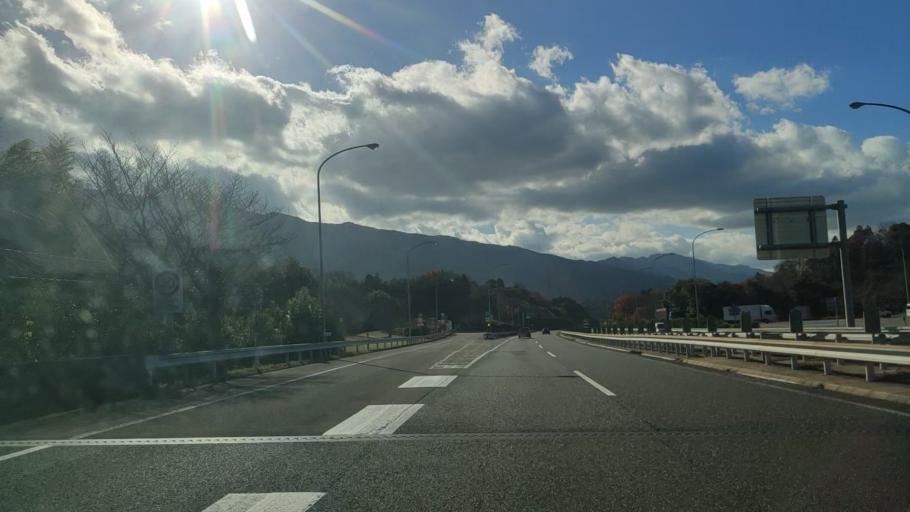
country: JP
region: Ehime
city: Kawanoecho
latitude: 33.9850
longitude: 133.5885
